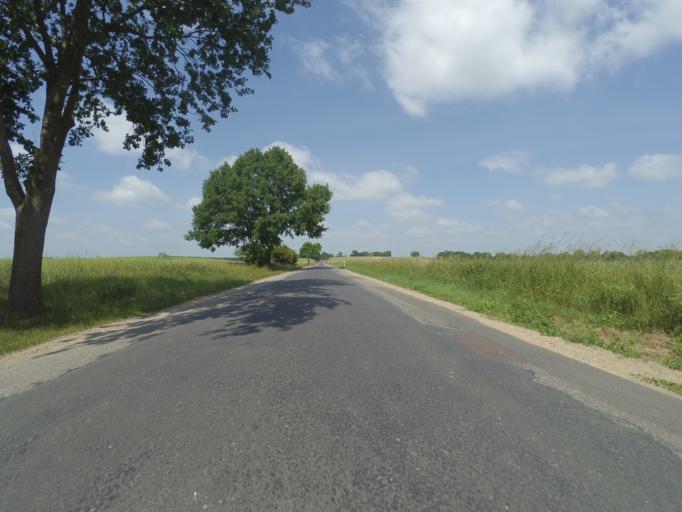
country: DE
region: Mecklenburg-Vorpommern
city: Lubz
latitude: 53.4099
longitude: 12.0136
